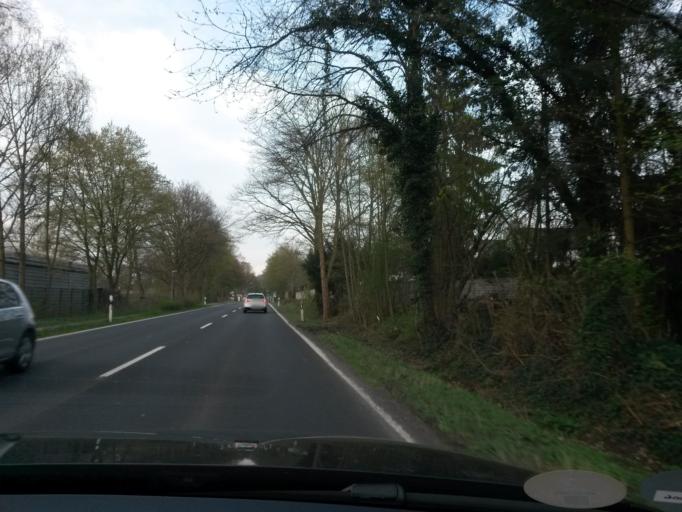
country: DE
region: North Rhine-Westphalia
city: Lohmar
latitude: 50.8545
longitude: 7.2279
